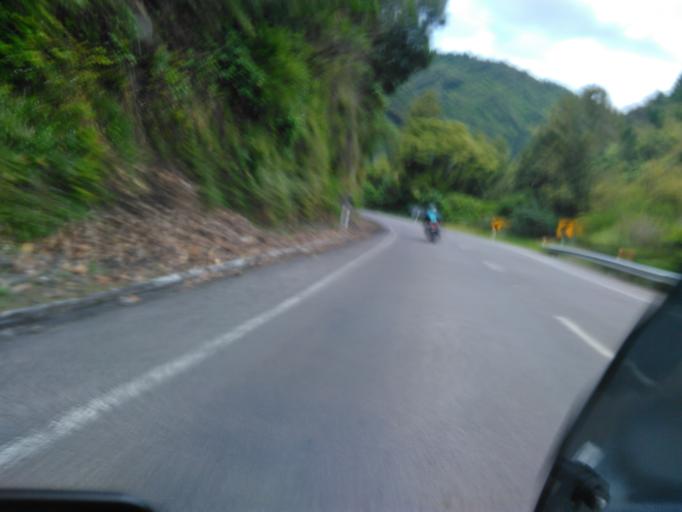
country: NZ
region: Bay of Plenty
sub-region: Opotiki District
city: Opotiki
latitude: -38.2697
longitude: 177.3068
